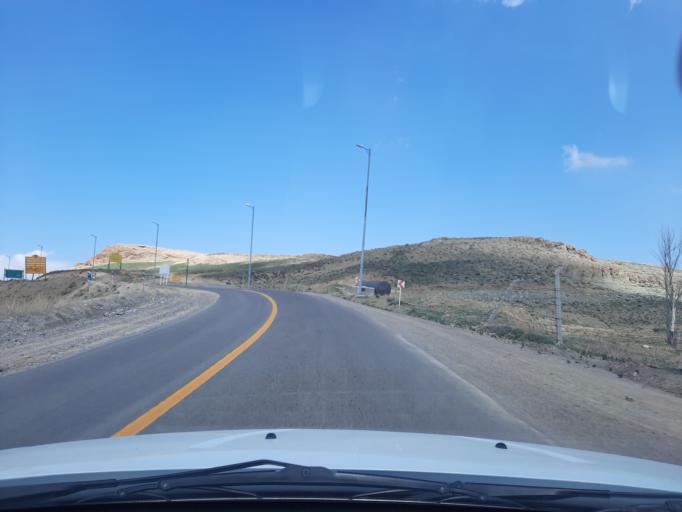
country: IR
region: Qazvin
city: Qazvin
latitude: 36.3842
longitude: 50.2062
